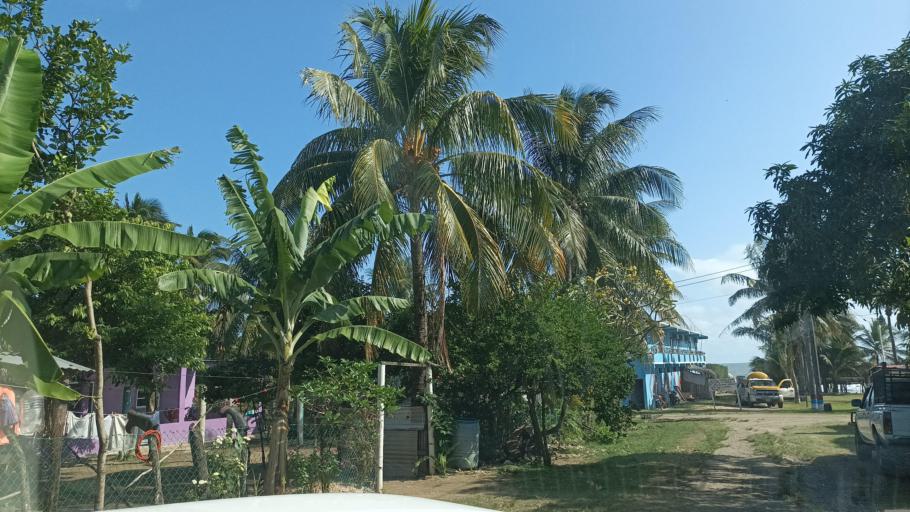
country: MX
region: Veracruz
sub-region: Coatzacoalcos
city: Fraccionamiento Ciudad Olmeca
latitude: 18.2126
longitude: -94.6116
